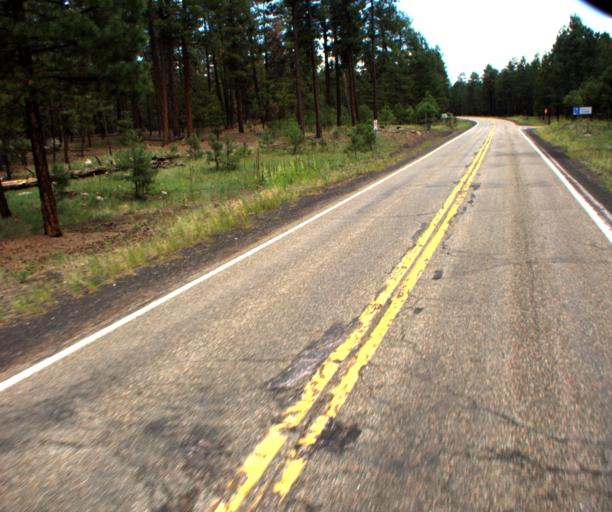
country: US
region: Arizona
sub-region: Coconino County
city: Flagstaff
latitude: 35.2873
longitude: -111.7605
